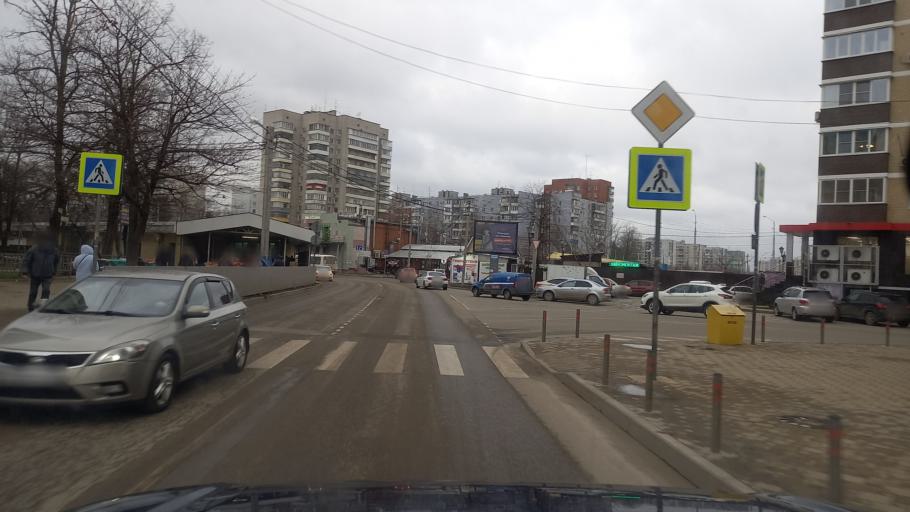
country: RU
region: Krasnodarskiy
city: Pashkovskiy
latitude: 45.0403
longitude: 39.0969
